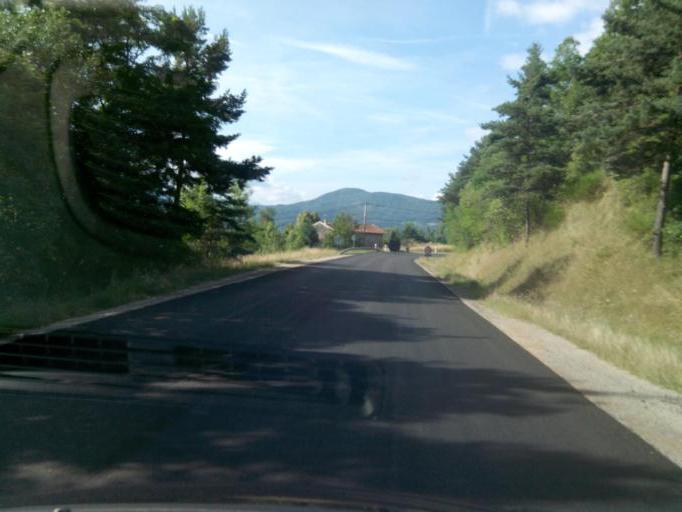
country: FR
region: Auvergne
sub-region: Departement de la Haute-Loire
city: Retournac
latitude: 45.2263
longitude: 4.0421
